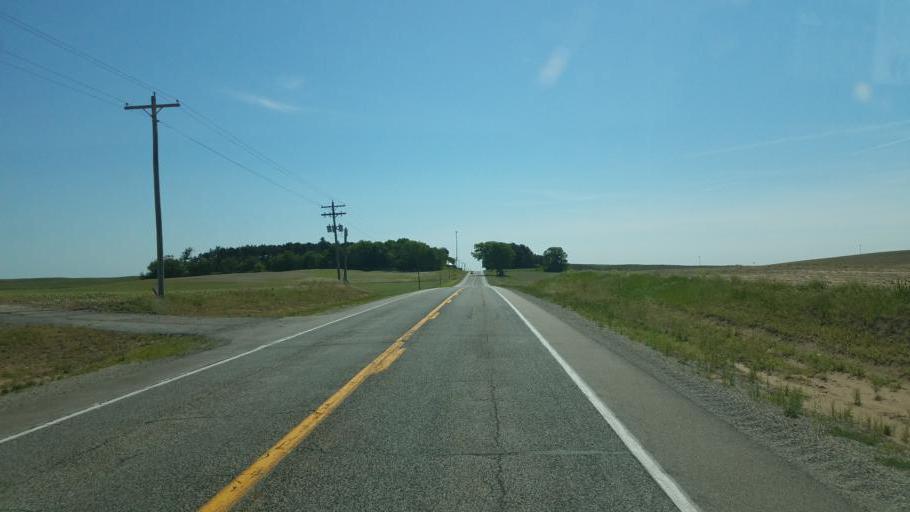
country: US
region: Illinois
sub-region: Mason County
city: Manito
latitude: 40.3034
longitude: -89.7865
